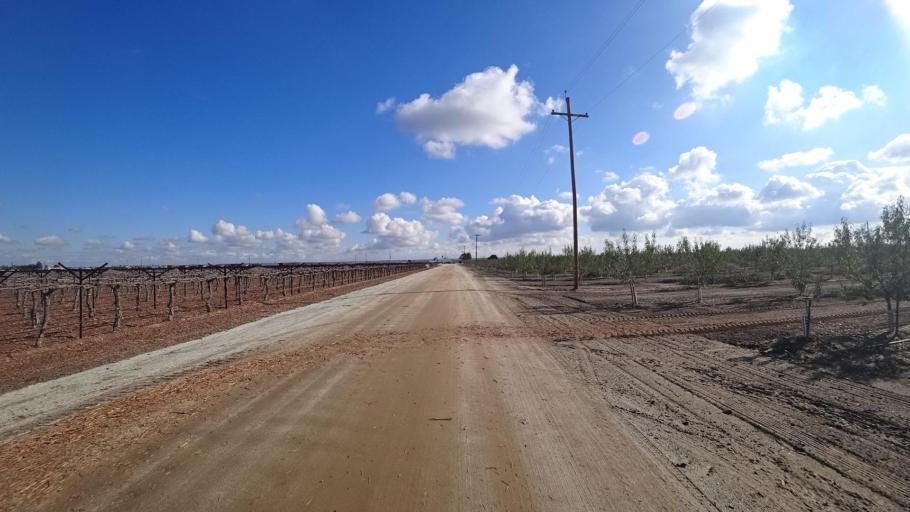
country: US
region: California
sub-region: Kern County
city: McFarland
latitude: 35.6599
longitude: -119.2270
